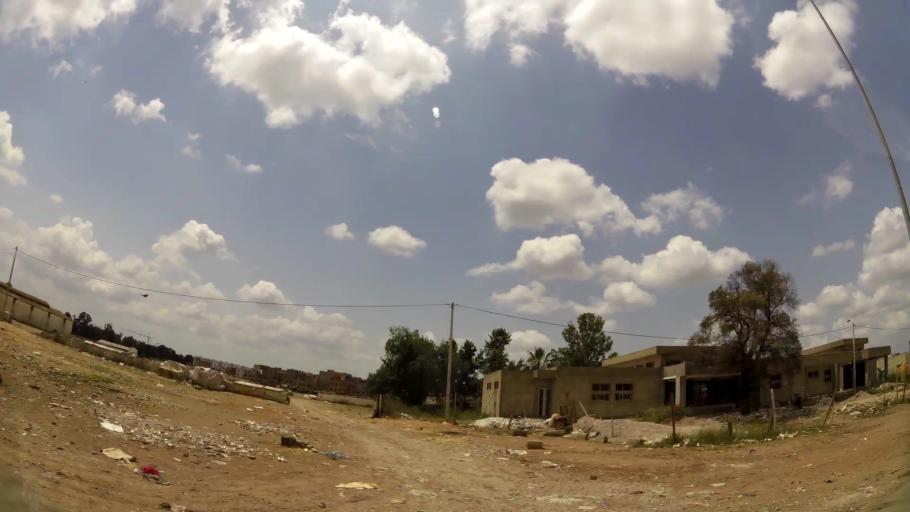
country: MA
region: Rabat-Sale-Zemmour-Zaer
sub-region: Khemisset
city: Tiflet
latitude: 34.0028
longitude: -6.5260
